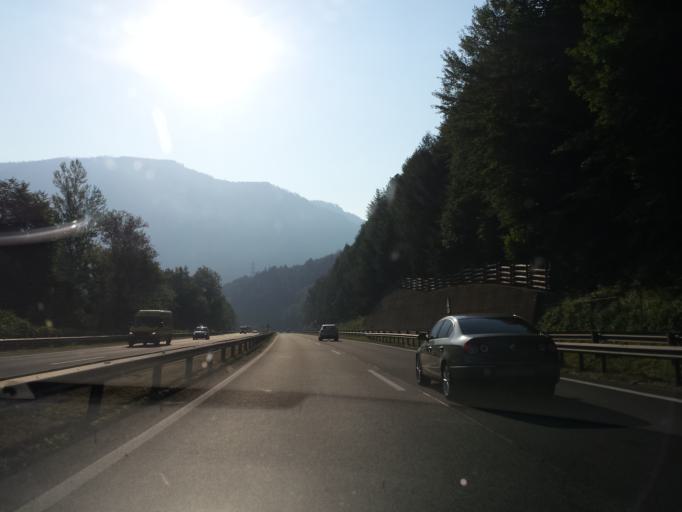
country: AT
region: Styria
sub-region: Politischer Bezirk Bruck-Muerzzuschlag
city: Bruck an der Mur
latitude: 47.3907
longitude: 15.2932
